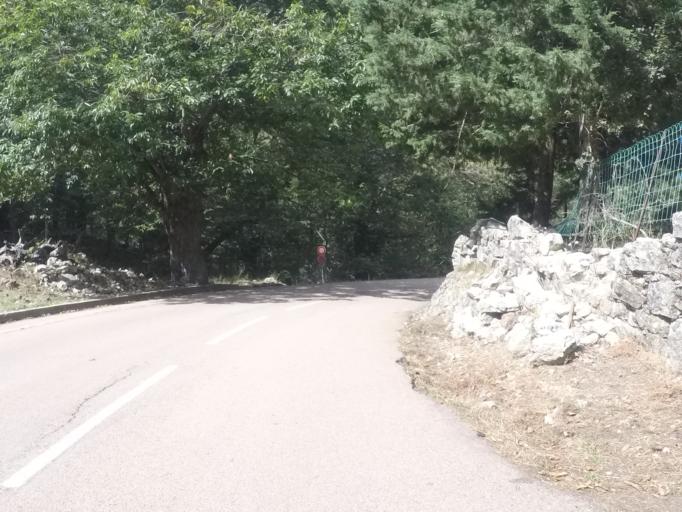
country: FR
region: Corsica
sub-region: Departement de la Corse-du-Sud
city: Zonza
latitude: 41.8104
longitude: 9.2460
